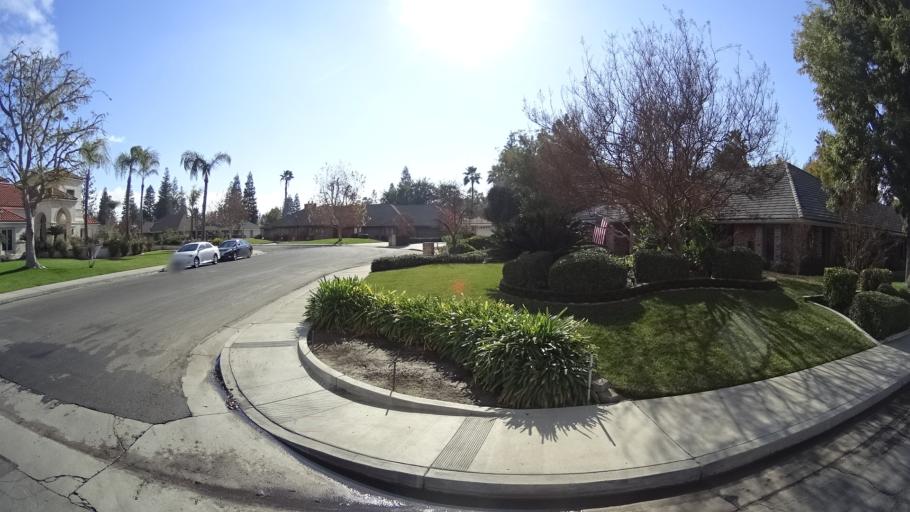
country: US
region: California
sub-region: Kern County
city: Greenacres
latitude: 35.3436
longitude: -119.0896
